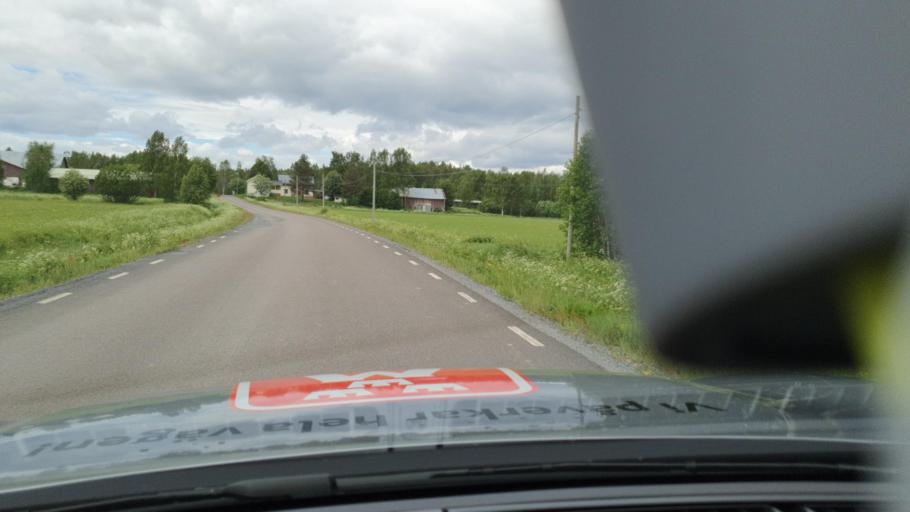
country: SE
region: Norrbotten
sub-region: Lulea Kommun
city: Sodra Sunderbyn
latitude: 65.8461
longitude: 21.9233
